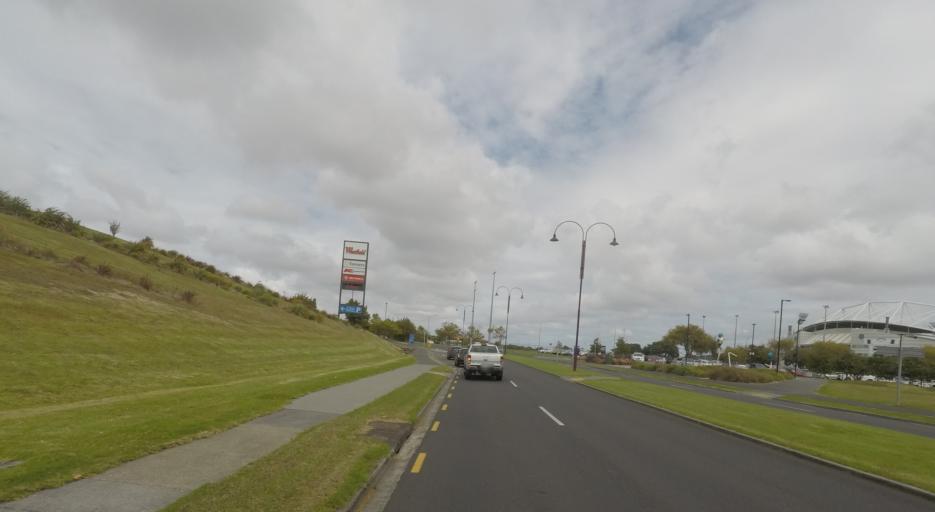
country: NZ
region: Auckland
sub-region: Auckland
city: Rothesay Bay
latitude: -36.7263
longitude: 174.7055
